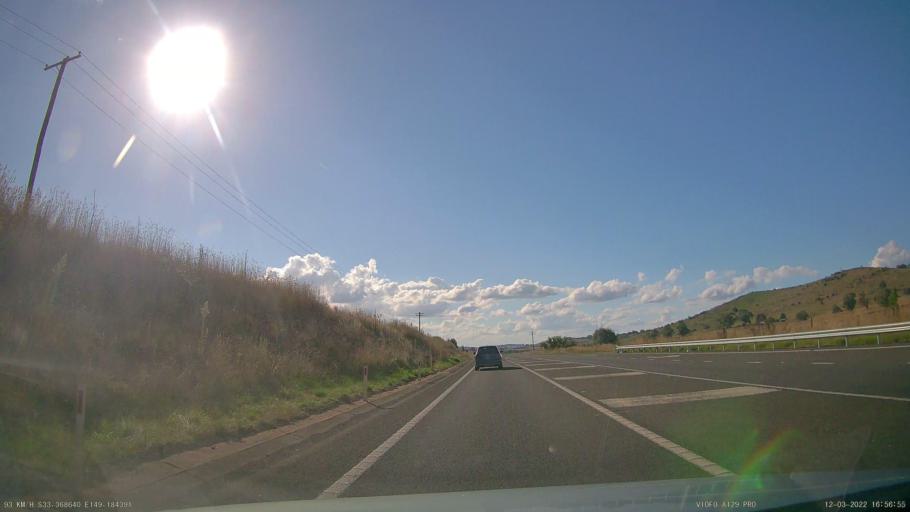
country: AU
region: New South Wales
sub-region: Blayney
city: Millthorpe
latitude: -33.3684
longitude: 149.1843
